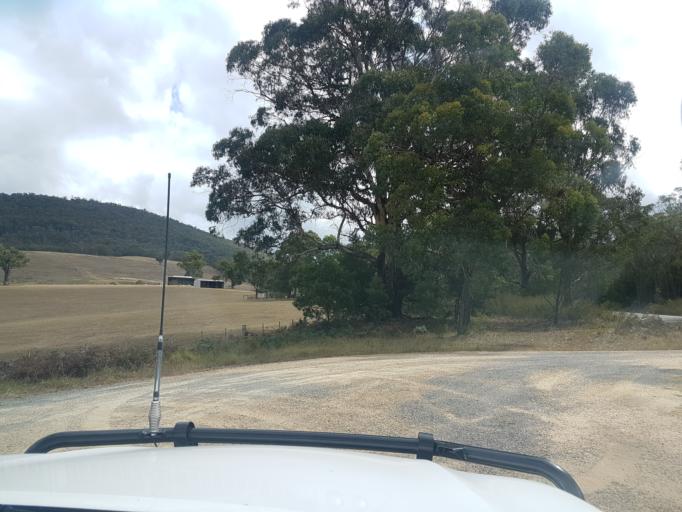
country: AU
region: Victoria
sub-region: East Gippsland
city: Bairnsdale
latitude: -37.6755
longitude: 147.5491
